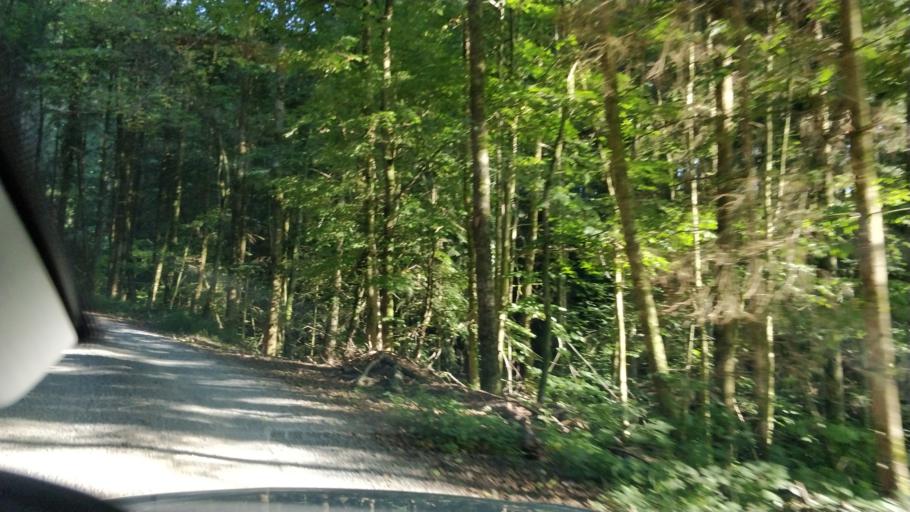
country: DE
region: Baden-Wuerttemberg
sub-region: Regierungsbezirk Stuttgart
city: Murrhardt
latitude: 49.0166
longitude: 9.5797
